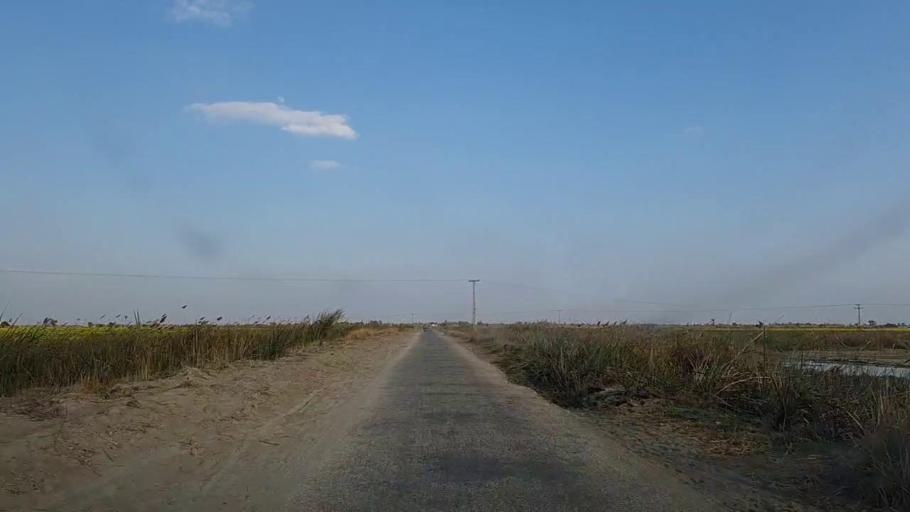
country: PK
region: Sindh
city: Sanghar
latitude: 26.2644
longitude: 68.9417
